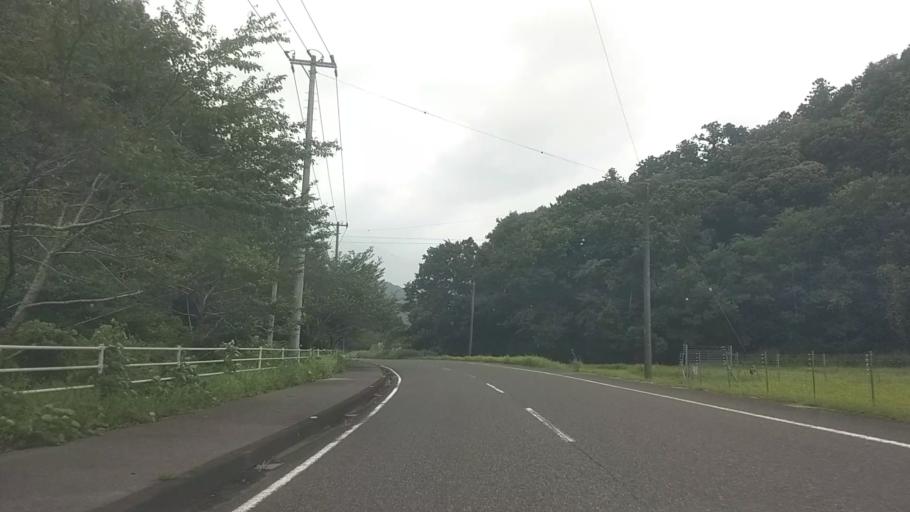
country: JP
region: Chiba
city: Kawaguchi
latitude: 35.2453
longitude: 140.0380
